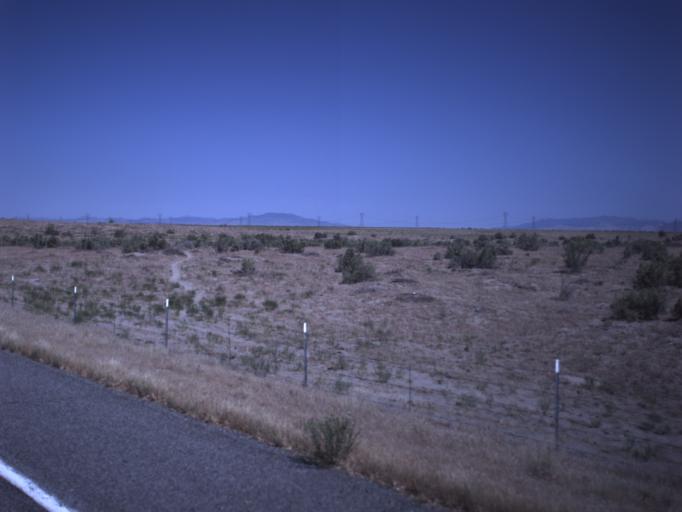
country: US
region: Utah
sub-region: Millard County
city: Delta
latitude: 39.4729
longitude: -112.4730
